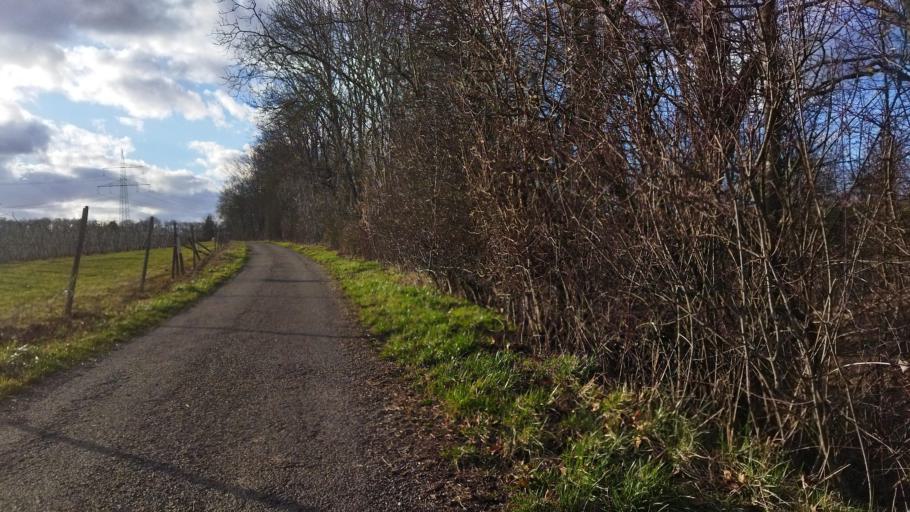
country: DE
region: Baden-Wuerttemberg
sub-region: Regierungsbezirk Stuttgart
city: Guglingen
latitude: 49.0814
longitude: 9.0105
